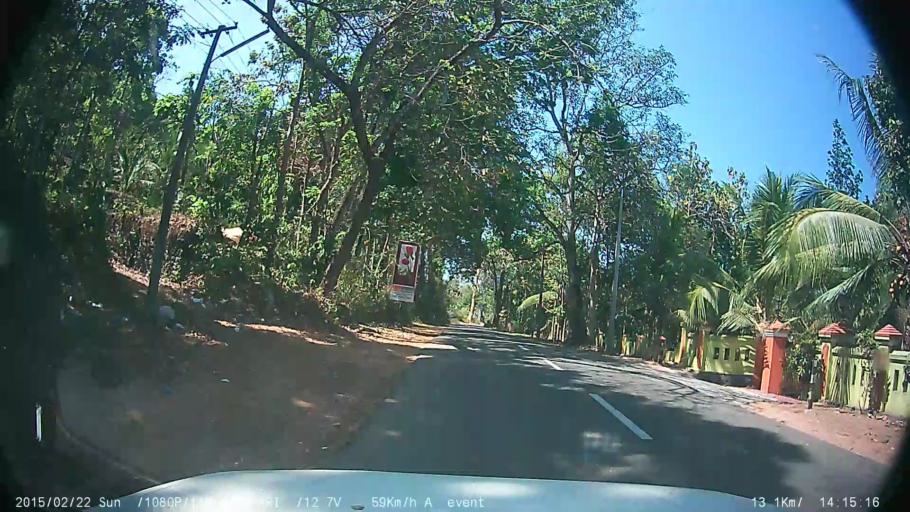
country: IN
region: Kerala
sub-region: Kottayam
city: Kottayam
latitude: 9.5483
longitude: 76.6843
